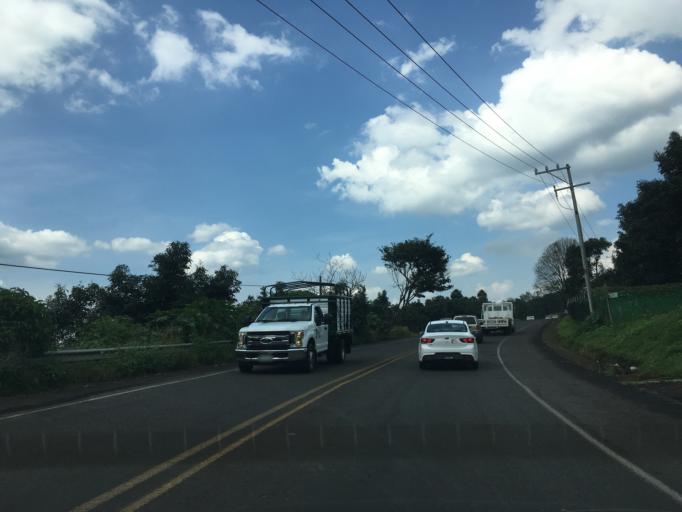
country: MX
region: Michoacan
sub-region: Tingueindin
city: Tingueindin
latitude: 19.7453
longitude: -102.4862
